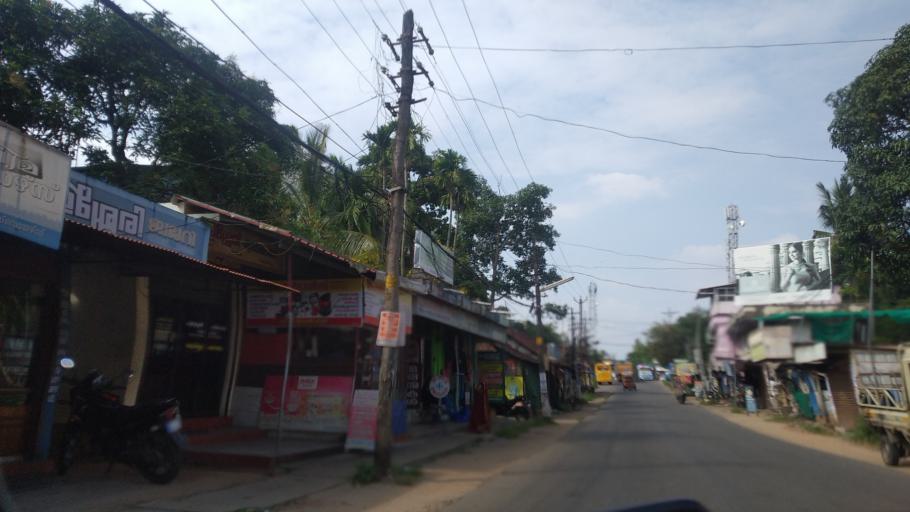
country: IN
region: Kerala
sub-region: Ernakulam
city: Elur
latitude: 10.0793
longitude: 76.2102
